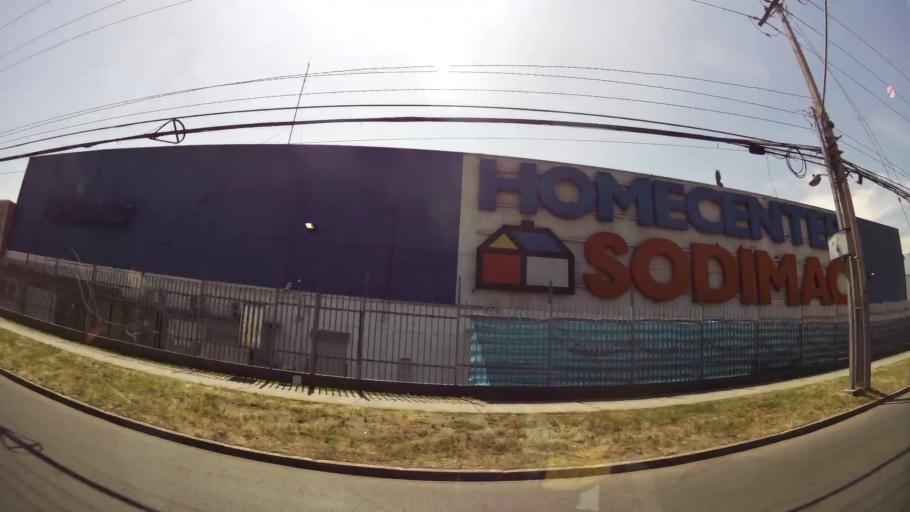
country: CL
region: Santiago Metropolitan
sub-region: Provincia de Santiago
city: Villa Presidente Frei, Nunoa, Santiago, Chile
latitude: -33.4635
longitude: -70.5453
